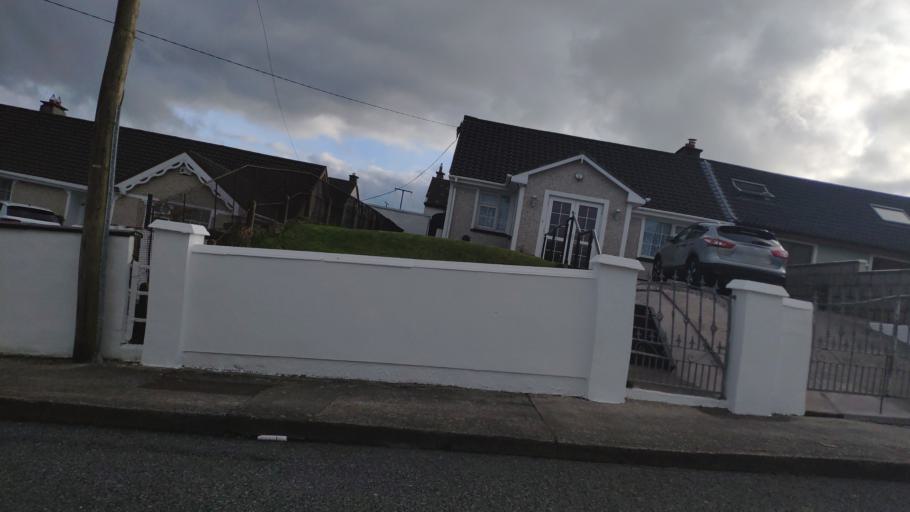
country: IE
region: Munster
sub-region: County Cork
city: Cork
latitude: 51.9085
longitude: -8.4836
